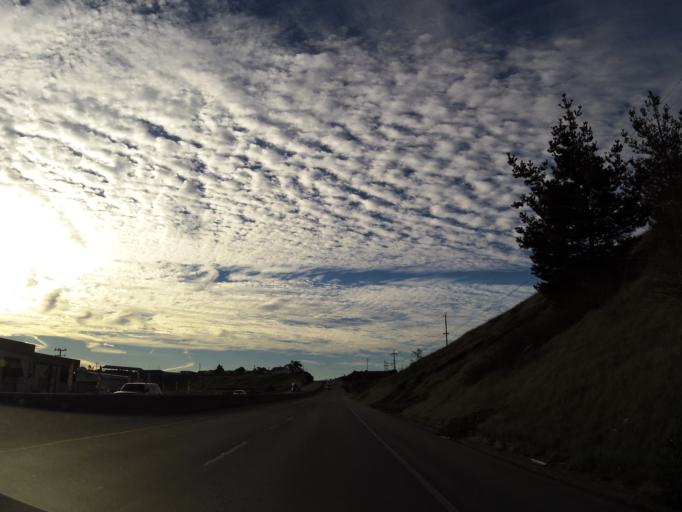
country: US
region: California
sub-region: Monterey County
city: Prunedale
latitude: 36.7567
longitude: -121.6654
